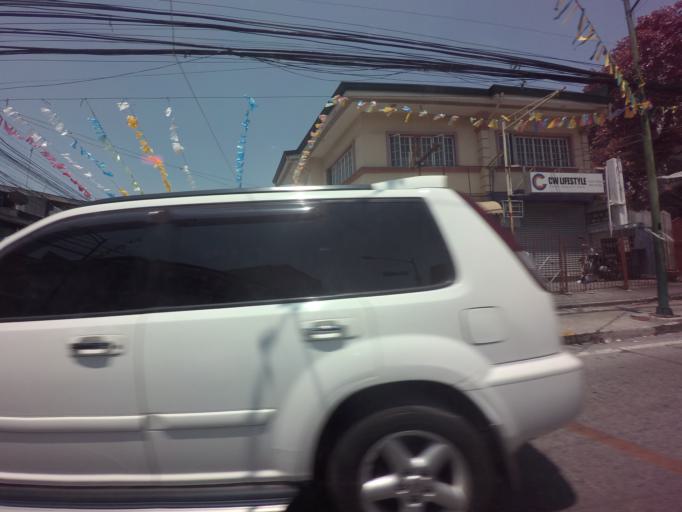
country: PH
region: Metro Manila
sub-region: Makati City
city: Makati City
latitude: 14.5622
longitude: 121.0020
